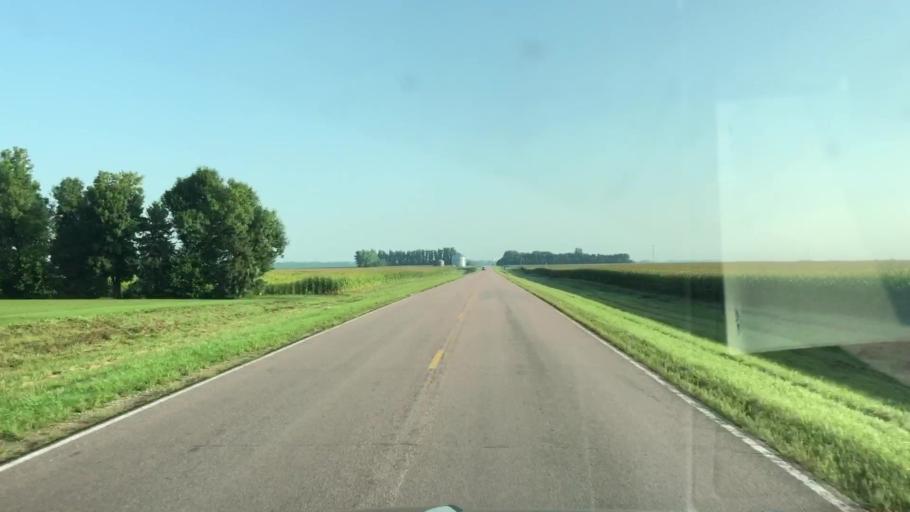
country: US
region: Iowa
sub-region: Lyon County
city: George
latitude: 43.3117
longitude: -95.9991
